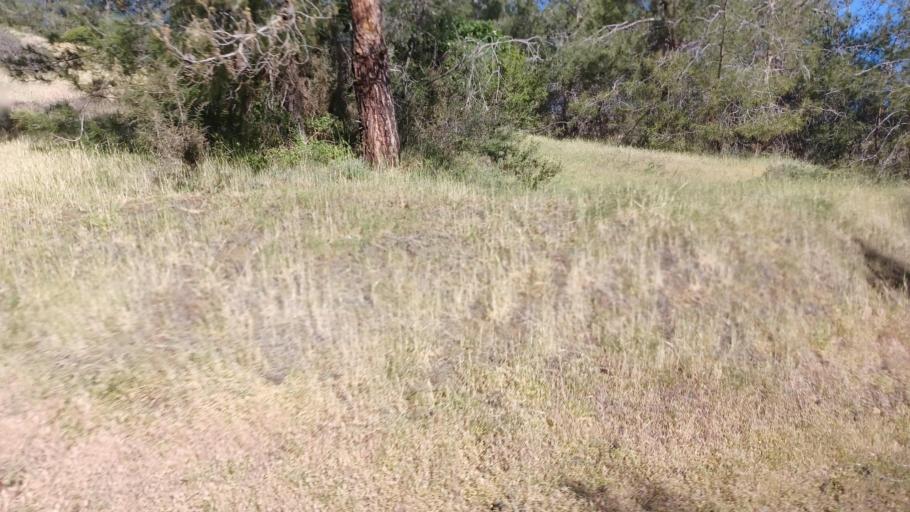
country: CY
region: Lefkosia
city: Peristerona
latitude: 35.0273
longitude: 33.0539
